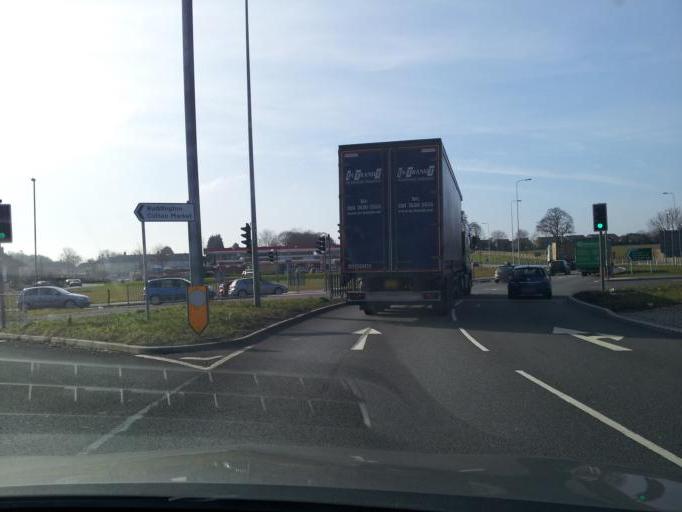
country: GB
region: England
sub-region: Nottinghamshire
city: Ruddington
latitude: 52.9074
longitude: -1.1871
